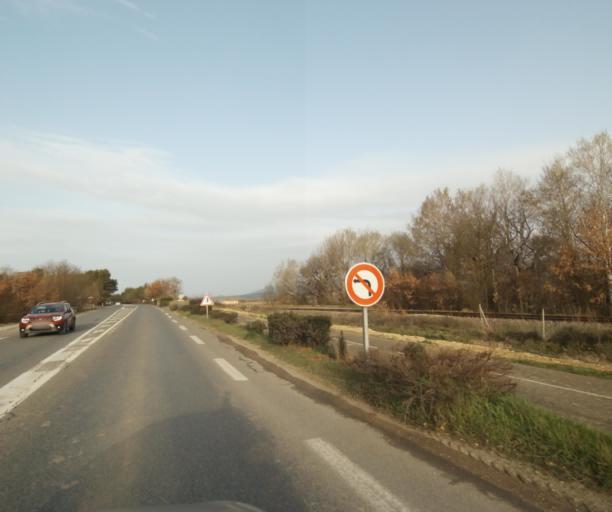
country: FR
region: Provence-Alpes-Cote d'Azur
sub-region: Departement des Bouches-du-Rhone
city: Peynier
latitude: 43.4584
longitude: 5.6539
